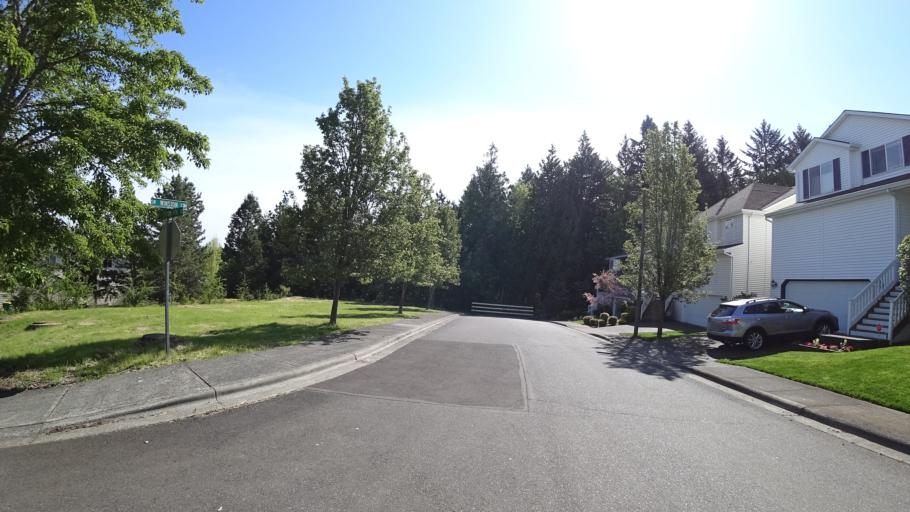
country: US
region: Oregon
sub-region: Washington County
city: Aloha
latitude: 45.4554
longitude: -122.8439
